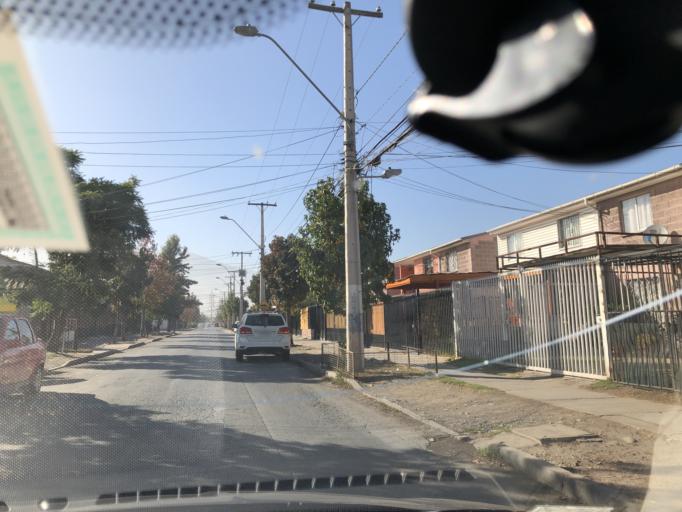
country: CL
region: Santiago Metropolitan
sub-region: Provincia de Santiago
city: La Pintana
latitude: -33.5763
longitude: -70.6034
